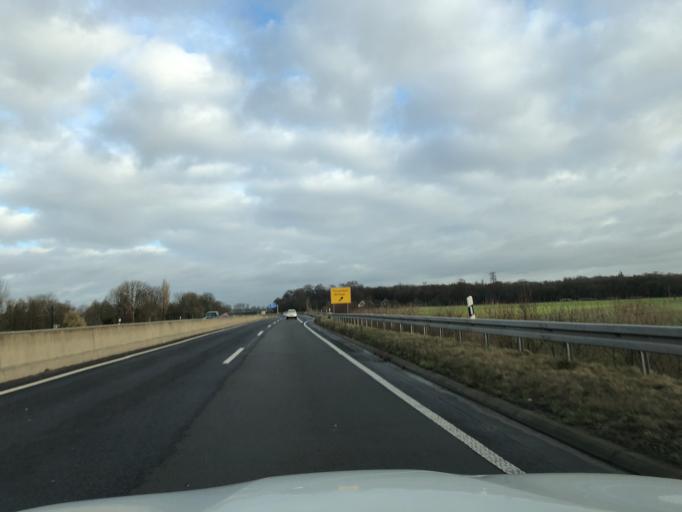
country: DE
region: North Rhine-Westphalia
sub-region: Regierungsbezirk Dusseldorf
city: Hochfeld
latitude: 51.3334
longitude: 6.7509
